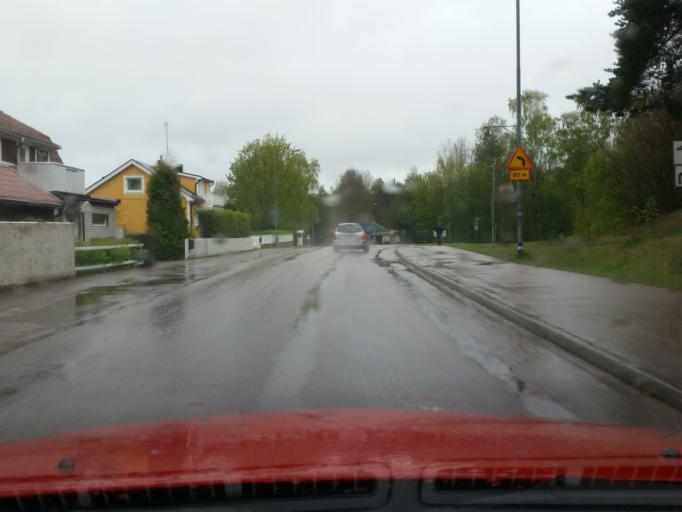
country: SE
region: Dalarna
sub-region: Hedemora Kommun
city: Hedemora
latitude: 60.2881
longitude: 15.9749
